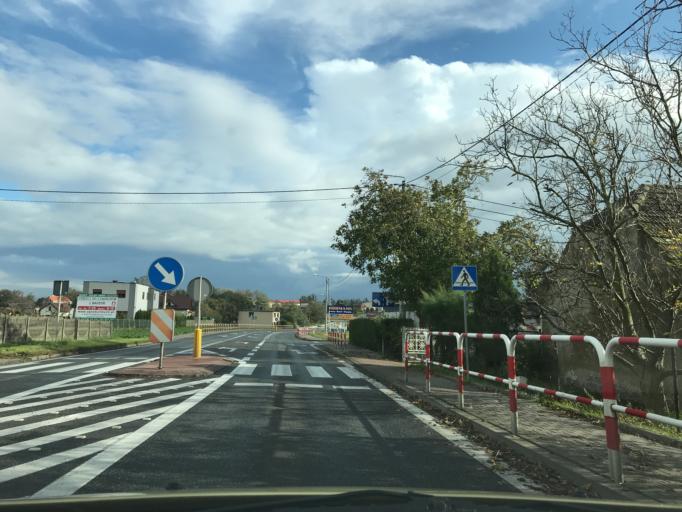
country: PL
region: Greater Poland Voivodeship
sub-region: Powiat ostrowski
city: Nowe Skalmierzyce
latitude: 51.7877
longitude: 18.0060
